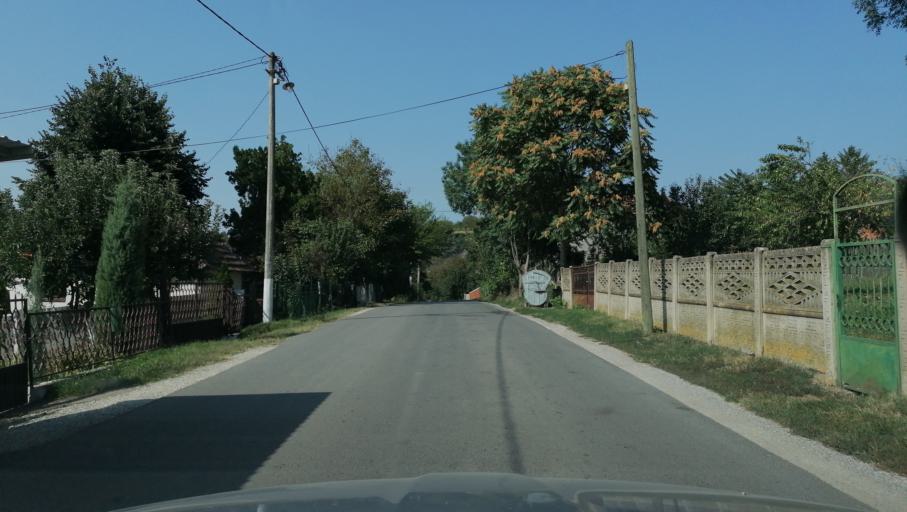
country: RS
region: Central Serbia
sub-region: Belgrade
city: Sopot
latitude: 44.5813
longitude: 20.6126
